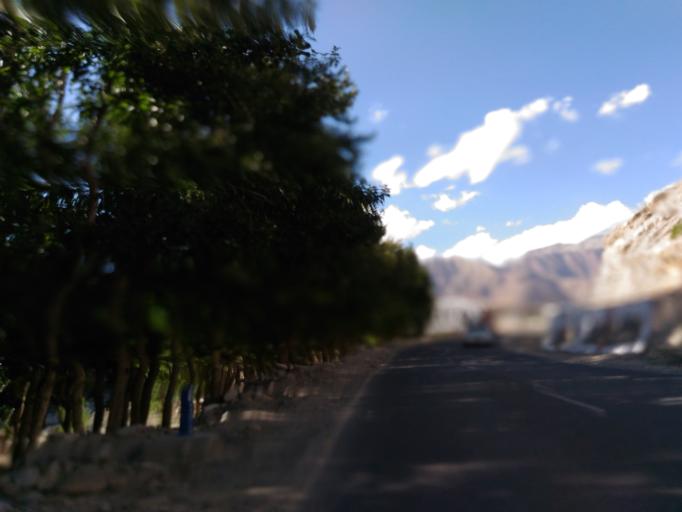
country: IN
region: Kashmir
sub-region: Ladakh
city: Leh
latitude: 34.1490
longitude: 77.4727
